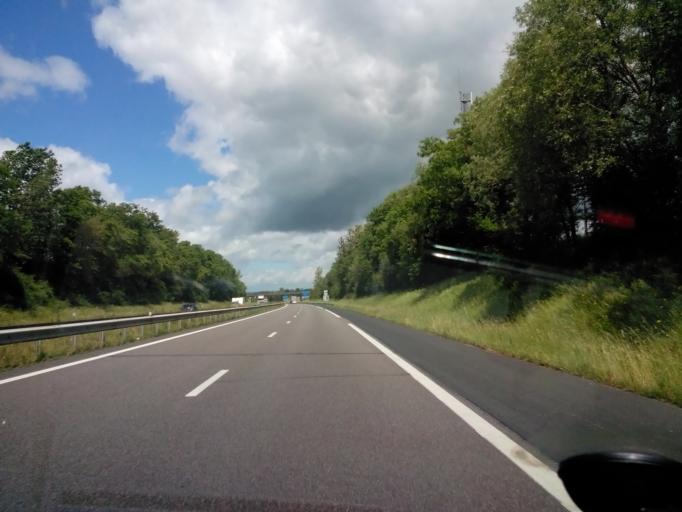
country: FR
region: Lorraine
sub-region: Departement des Vosges
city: Bulgneville
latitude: 48.2552
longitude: 5.8652
